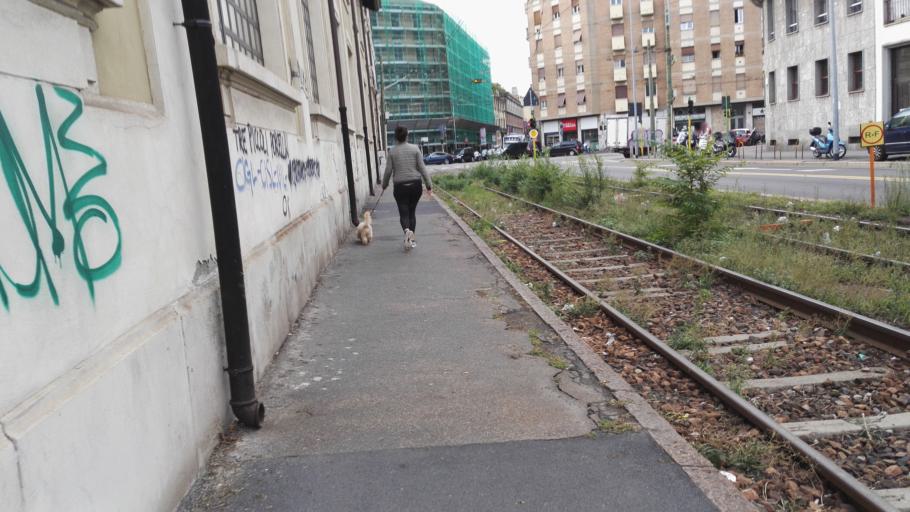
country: IT
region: Lombardy
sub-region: Citta metropolitana di Milano
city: Milano
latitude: 45.4845
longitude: 9.1745
